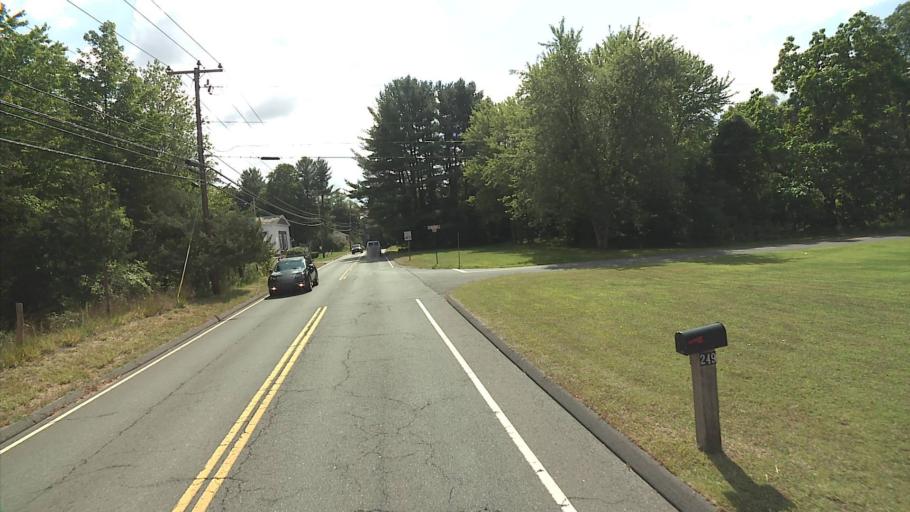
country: US
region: Connecticut
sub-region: Hartford County
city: North Granby
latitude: 41.9800
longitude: -72.8174
